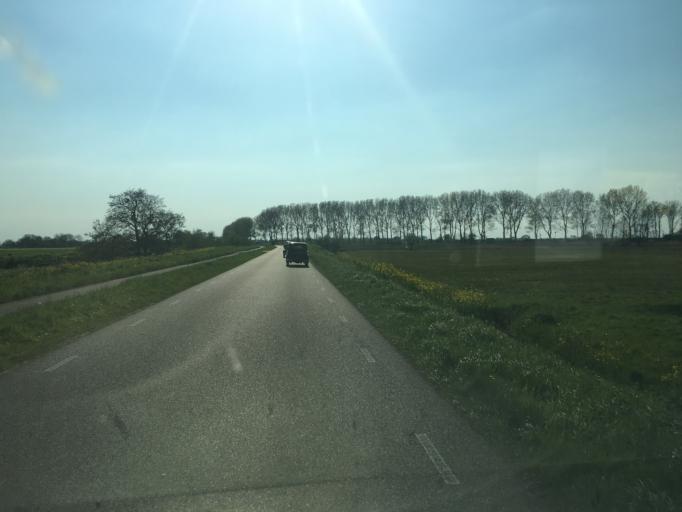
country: NL
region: Friesland
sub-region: Sudwest Fryslan
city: Koudum
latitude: 52.9461
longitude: 5.4274
